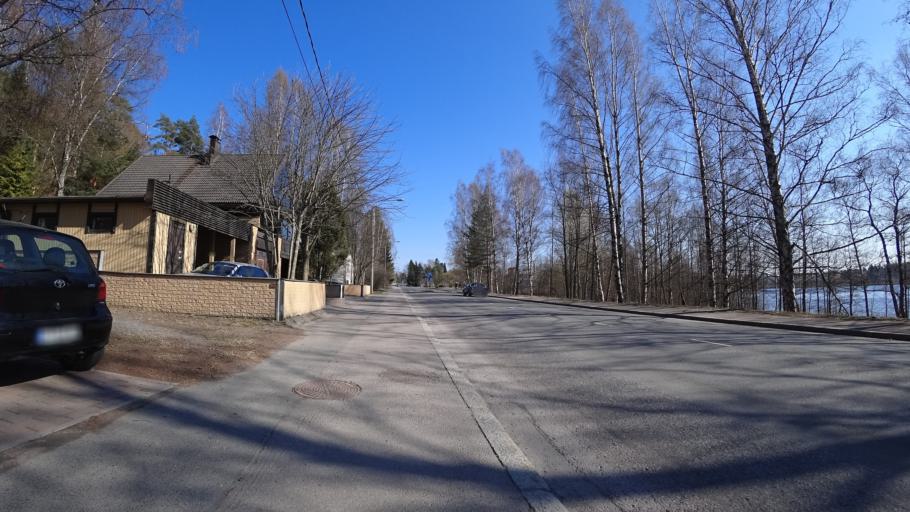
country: FI
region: Pirkanmaa
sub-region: Tampere
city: Pirkkala
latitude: 61.5124
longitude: 23.6583
